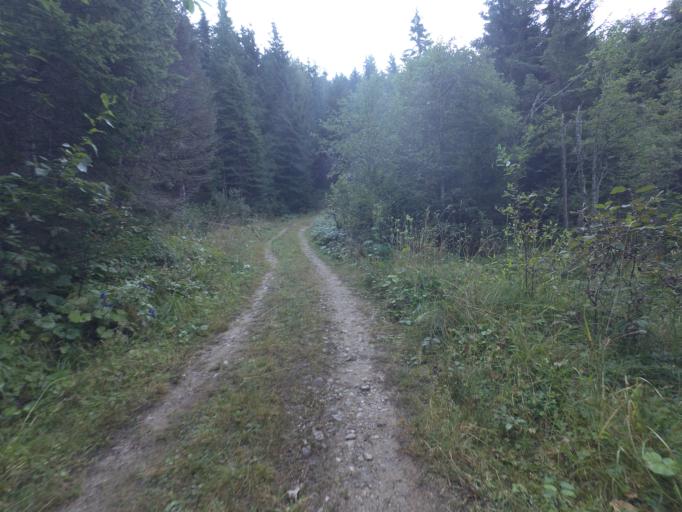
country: AT
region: Salzburg
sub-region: Politischer Bezirk Sankt Johann im Pongau
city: Kleinarl
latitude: 47.2719
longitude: 13.2634
